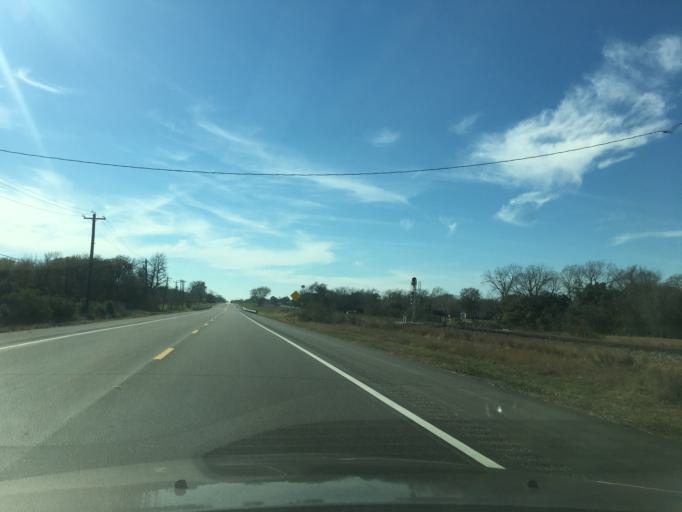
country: US
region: Texas
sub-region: Wharton County
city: East Bernard
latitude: 29.4530
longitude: -95.9911
